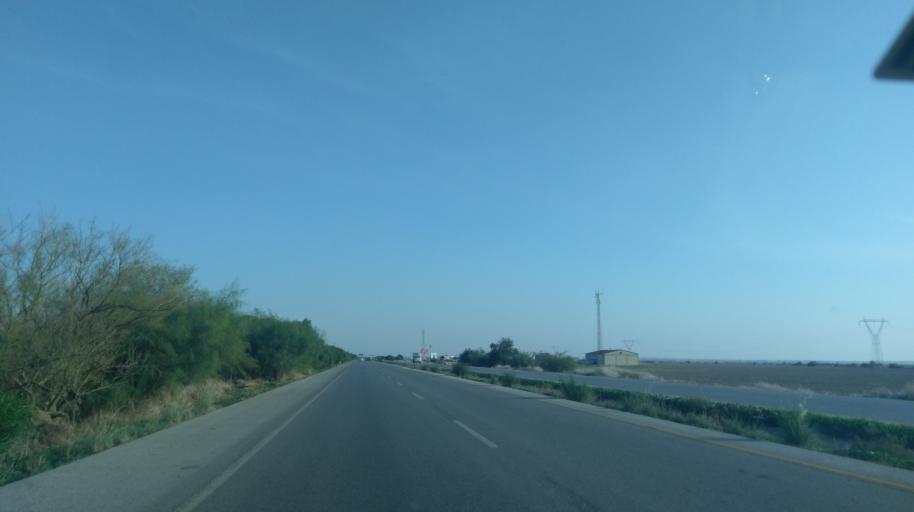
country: CY
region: Ammochostos
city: Acheritou
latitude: 35.1614
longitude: 33.8328
